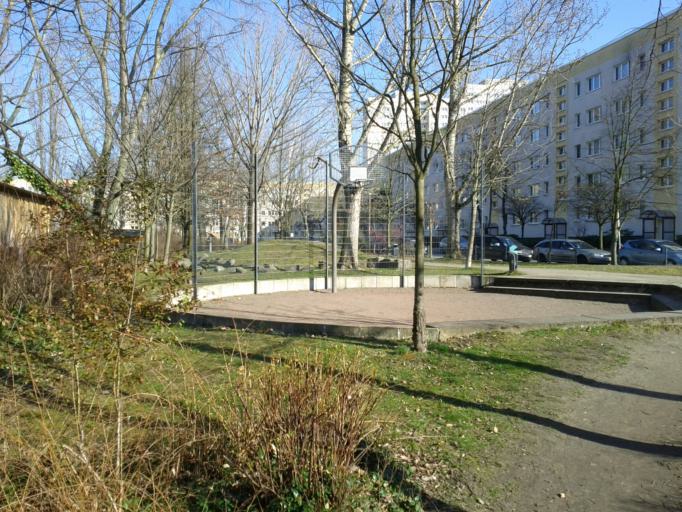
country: DE
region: Berlin
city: Friedrichsfelde
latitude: 52.5123
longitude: 13.5262
